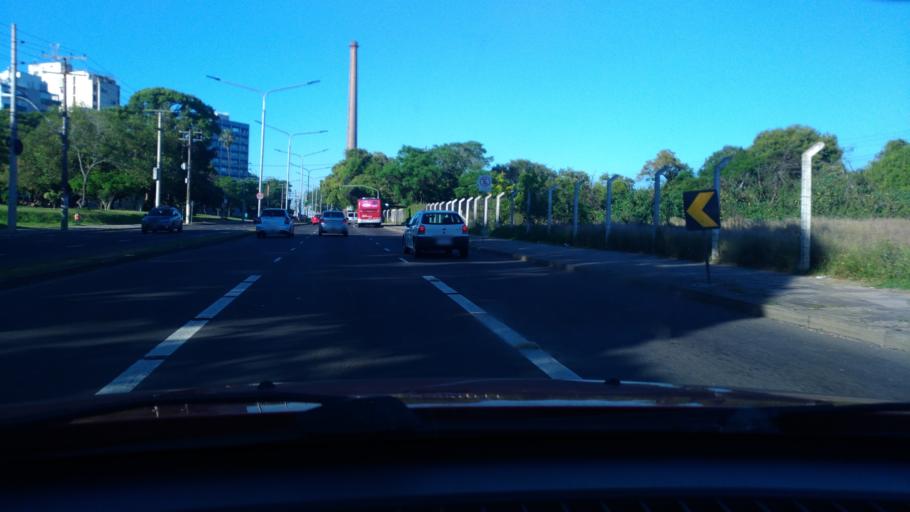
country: BR
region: Rio Grande do Sul
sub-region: Porto Alegre
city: Porto Alegre
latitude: -30.0312
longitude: -51.2386
